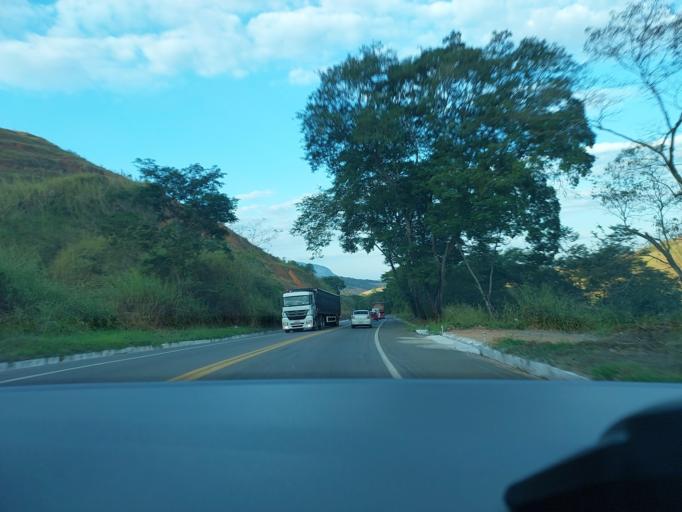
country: BR
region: Minas Gerais
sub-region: Muriae
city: Muriae
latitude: -21.1234
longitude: -42.2284
